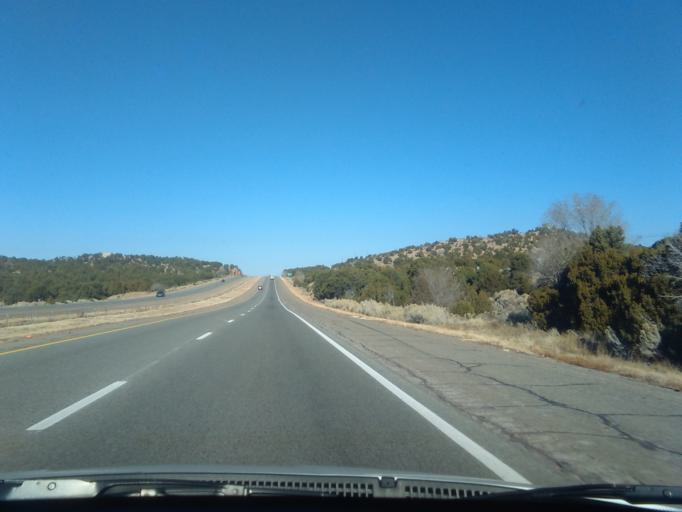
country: US
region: New Mexico
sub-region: Santa Fe County
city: Eldorado at Santa Fe
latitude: 35.6066
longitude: -105.9125
